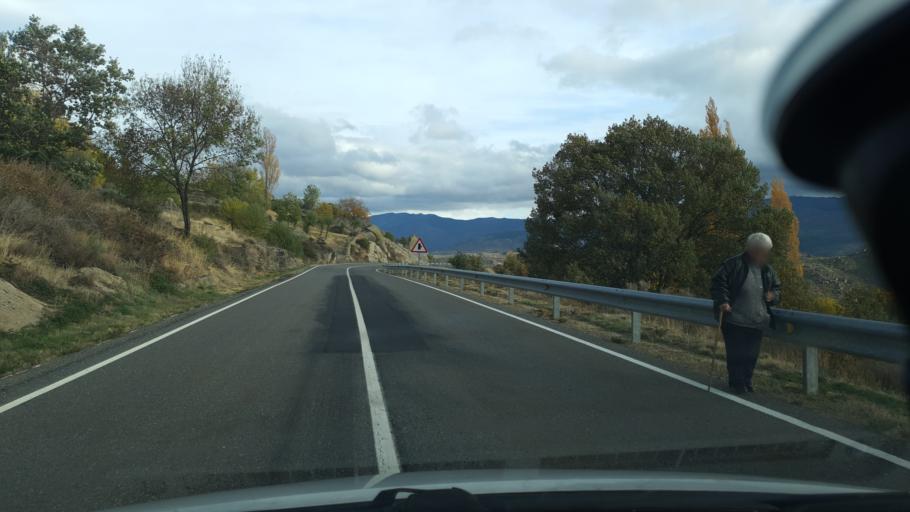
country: ES
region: Castille and Leon
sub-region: Provincia de Avila
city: Navalosa
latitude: 40.3963
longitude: -4.9251
